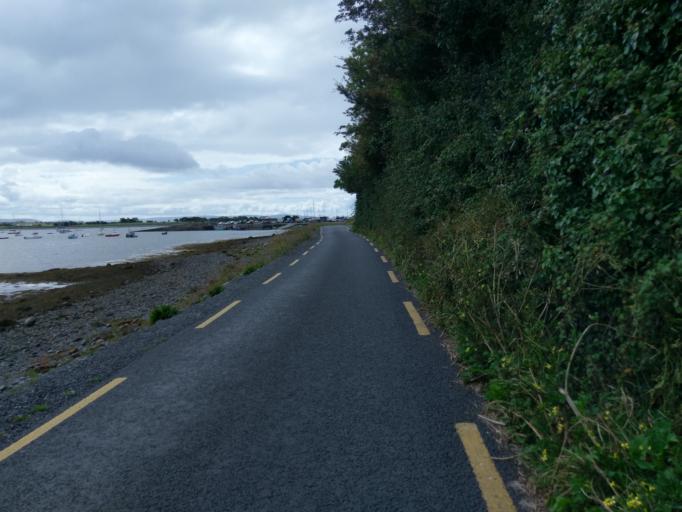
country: IE
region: Connaught
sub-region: County Galway
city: Oranmore
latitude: 53.2459
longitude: -8.9637
